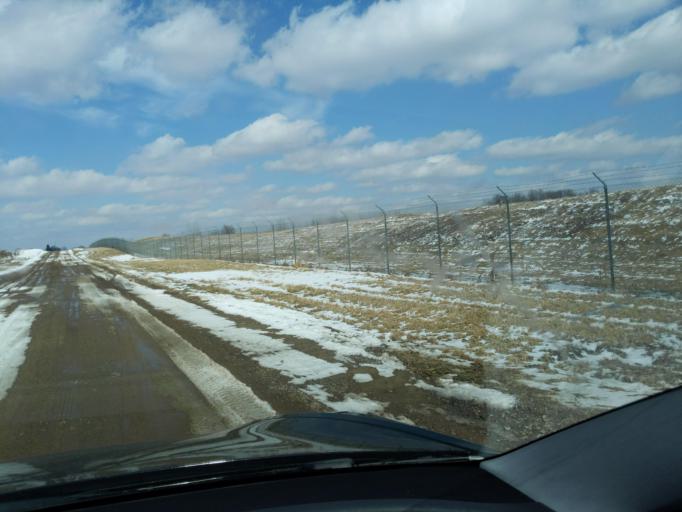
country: US
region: Michigan
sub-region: Livingston County
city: Fowlerville
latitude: 42.6141
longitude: -84.0616
